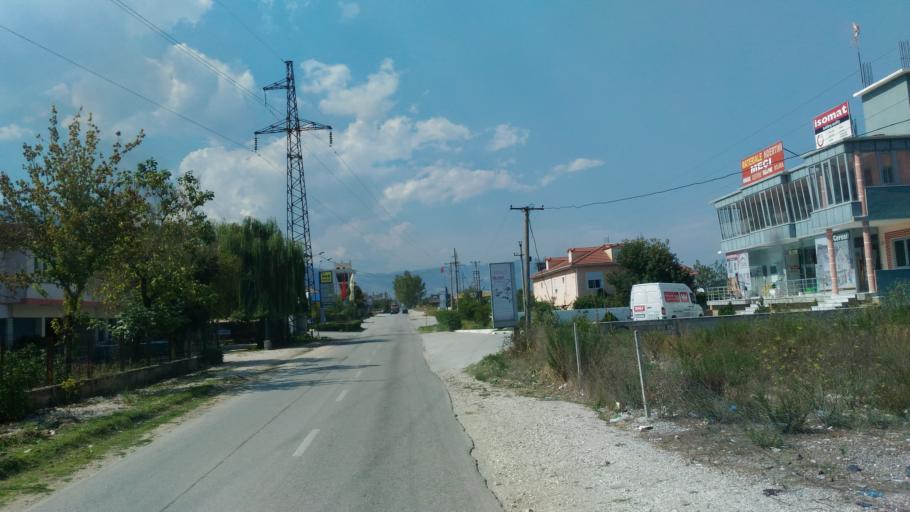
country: AL
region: Gjirokaster
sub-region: Rrethi i Gjirokastres
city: Lazarat
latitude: 40.0661
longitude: 20.1646
